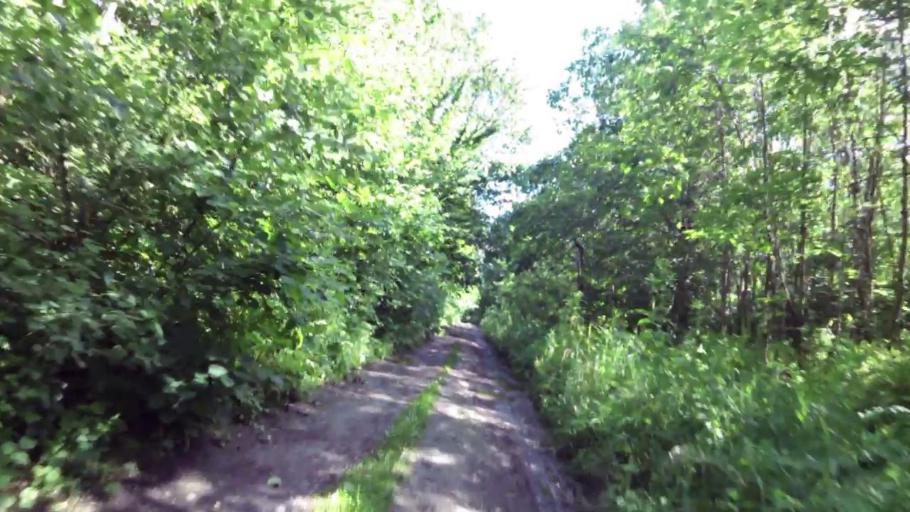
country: PL
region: West Pomeranian Voivodeship
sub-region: Powiat slawienski
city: Slawno
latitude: 54.5065
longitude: 16.7044
